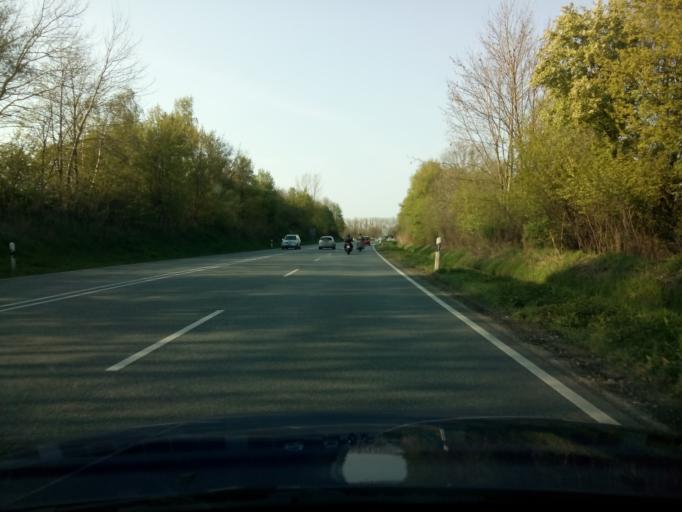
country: DE
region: Lower Saxony
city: Stuhr
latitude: 53.0136
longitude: 8.7984
